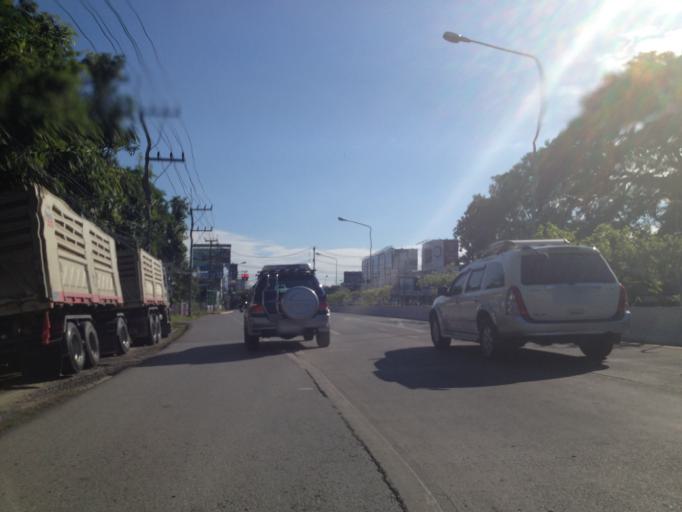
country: TH
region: Chiang Mai
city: Chiang Mai
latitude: 18.7924
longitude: 98.9614
